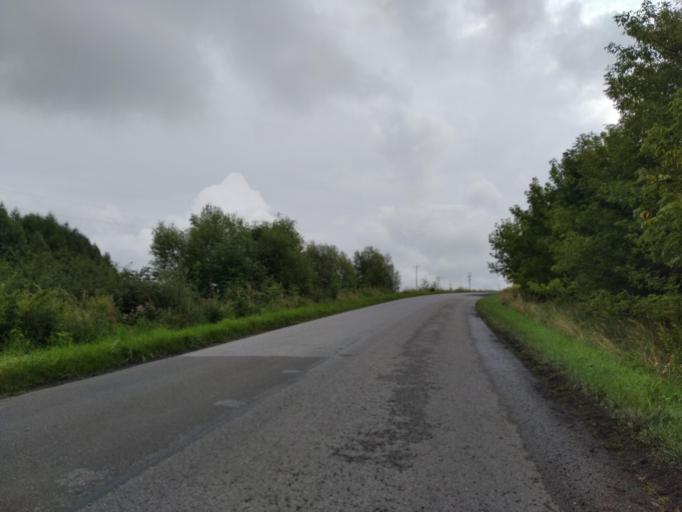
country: PL
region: Subcarpathian Voivodeship
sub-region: Powiat rzeszowski
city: Dynow
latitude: 49.7216
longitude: 22.3162
